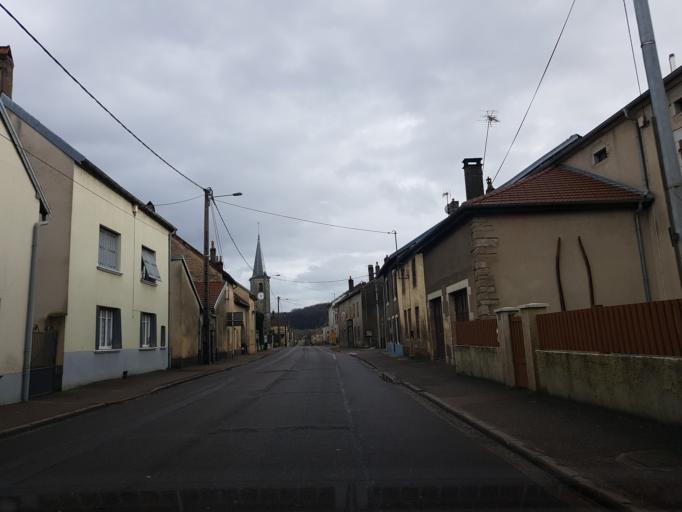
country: FR
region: Franche-Comte
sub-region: Departement de la Haute-Saone
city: Scey-sur-Saone-et-Saint-Albin
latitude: 47.7116
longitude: 5.8886
